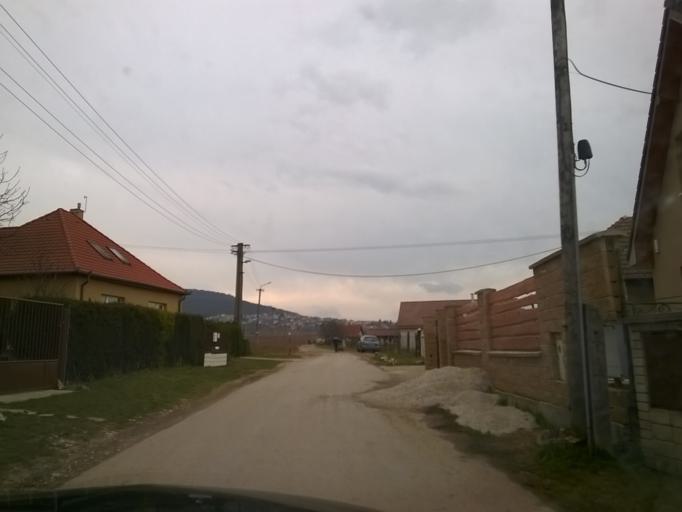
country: SK
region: Nitriansky
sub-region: Okres Nitra
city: Nitra
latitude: 48.3497
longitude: 18.0636
